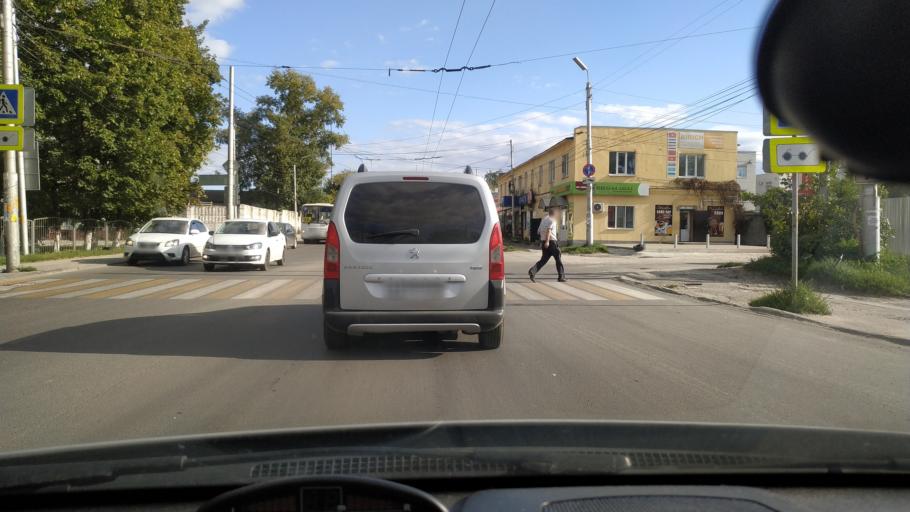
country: RU
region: Rjazan
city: Ryazan'
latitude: 54.6153
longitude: 39.6940
